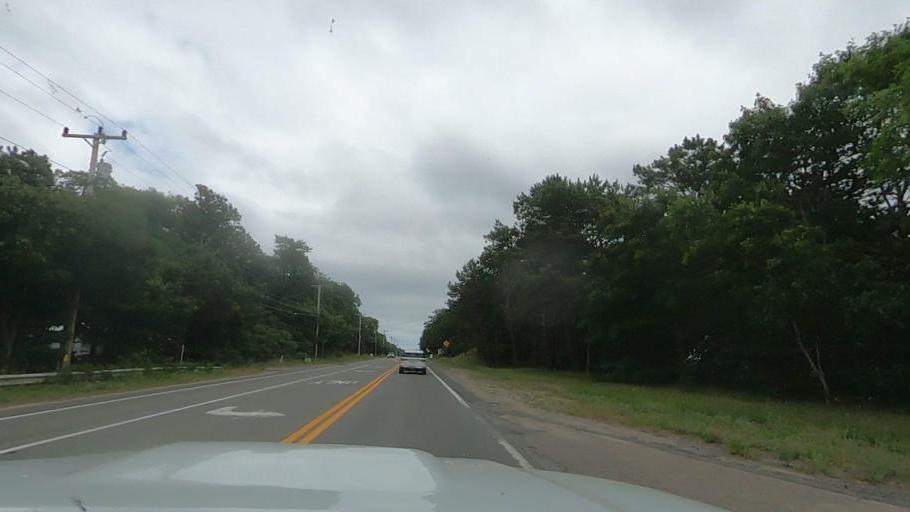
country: US
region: Massachusetts
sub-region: Barnstable County
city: Wellfleet
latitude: 41.9287
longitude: -70.0159
